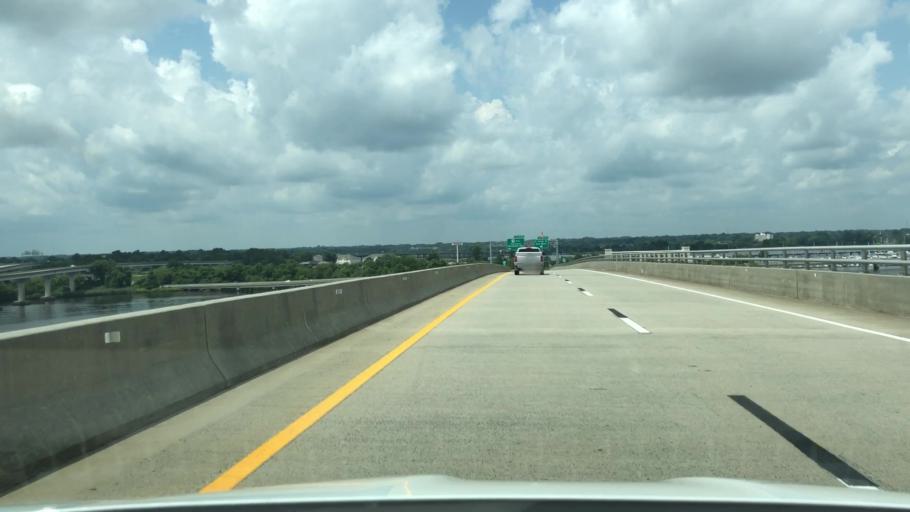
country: US
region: North Carolina
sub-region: Craven County
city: James City
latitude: 35.0968
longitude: -77.0313
